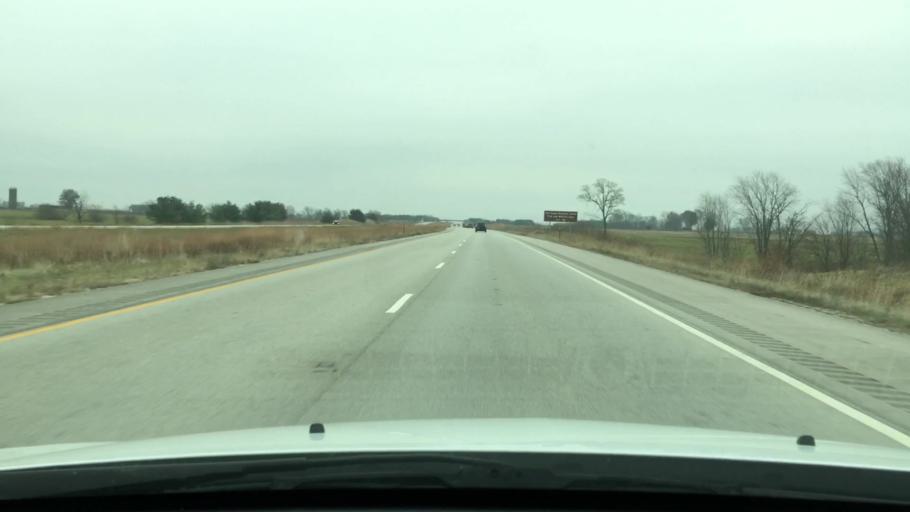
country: US
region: Illinois
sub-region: Sangamon County
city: New Berlin
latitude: 39.7367
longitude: -90.0652
